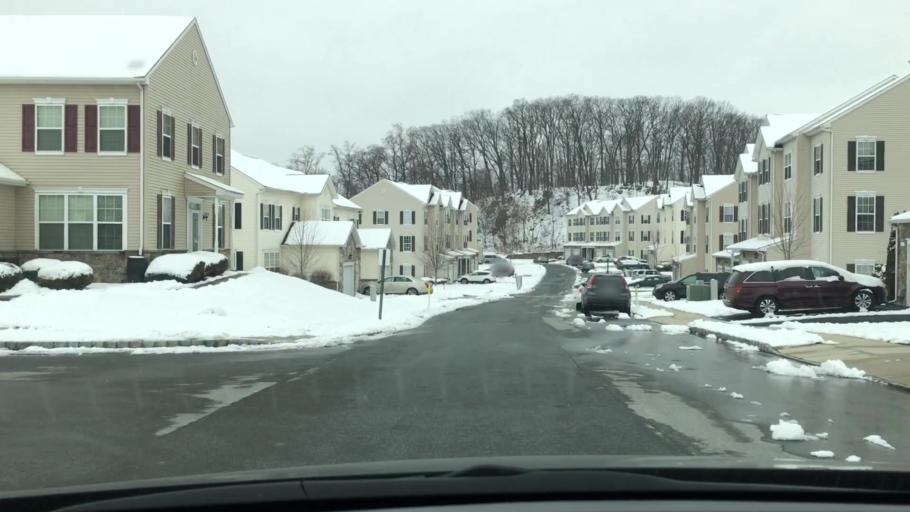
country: US
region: Pennsylvania
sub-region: York County
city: North York
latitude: 39.9961
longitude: -76.7152
